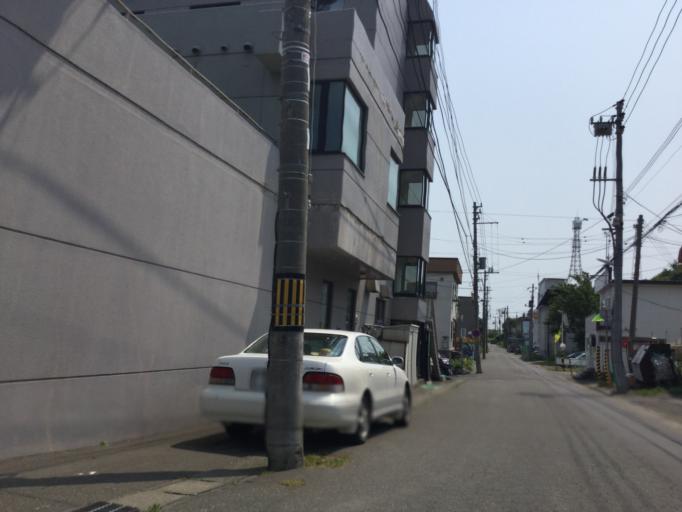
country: JP
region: Hokkaido
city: Wakkanai
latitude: 45.3994
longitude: 141.6790
